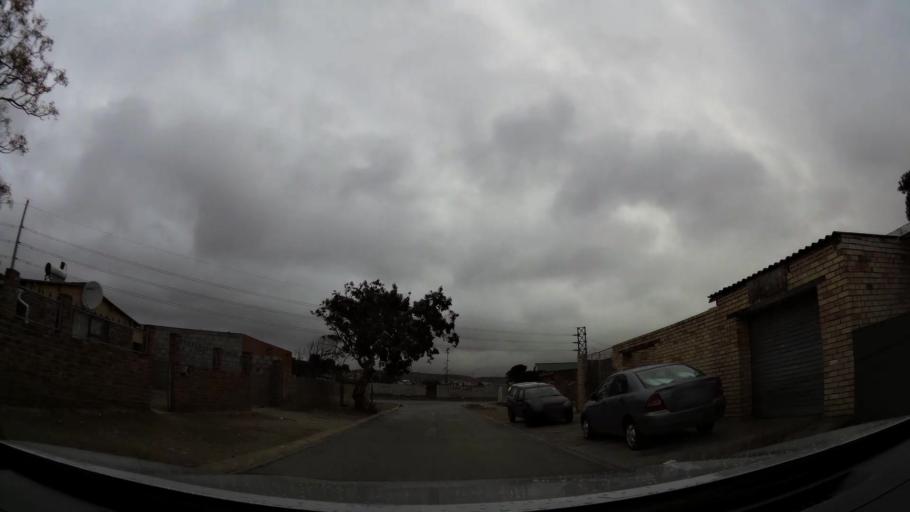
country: ZA
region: Eastern Cape
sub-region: Nelson Mandela Bay Metropolitan Municipality
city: Port Elizabeth
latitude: -33.8963
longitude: 25.5413
